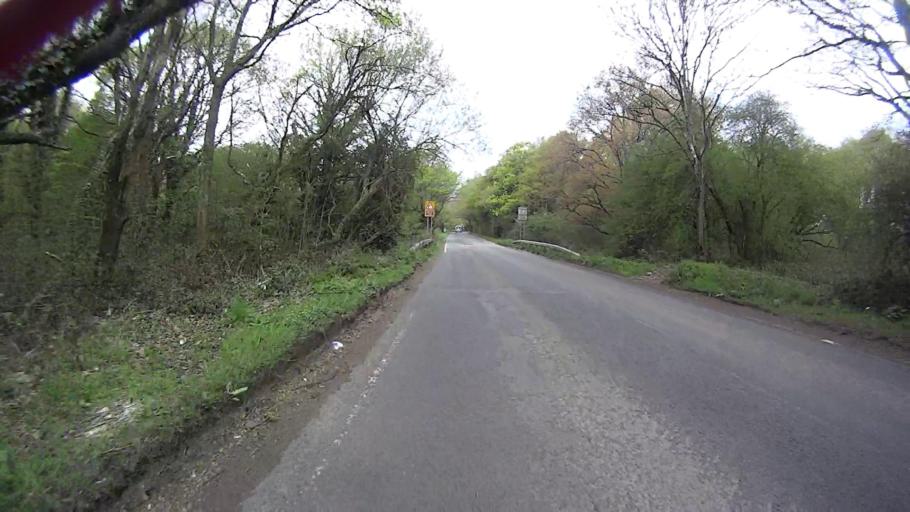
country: GB
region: England
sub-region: West Sussex
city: Gossops Green
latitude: 51.1361
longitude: -0.2255
